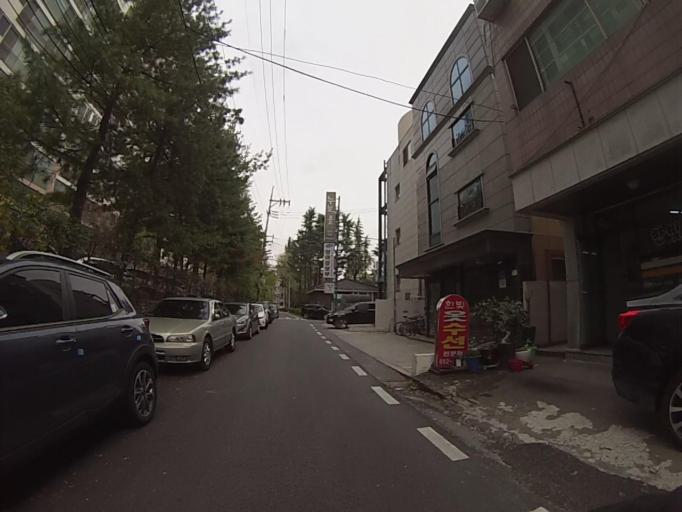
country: KR
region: Daejeon
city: Songgang-dong
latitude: 36.3613
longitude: 127.3548
